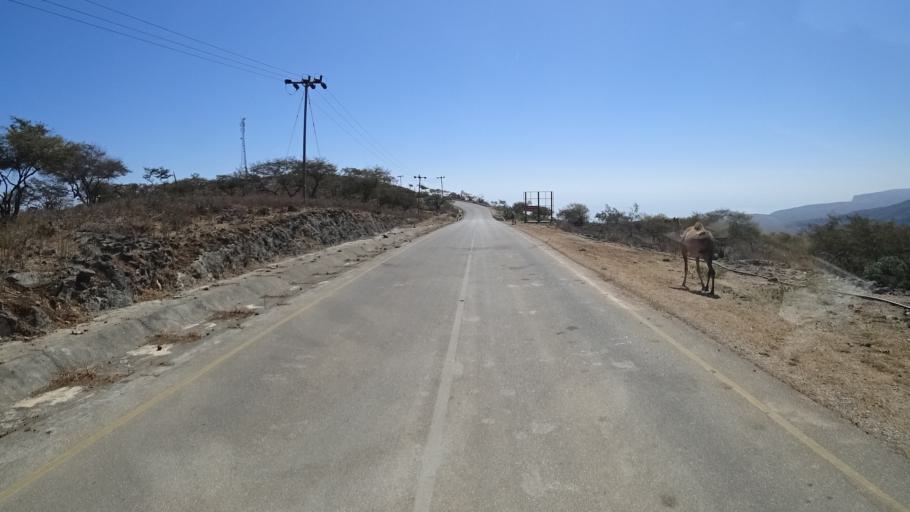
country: YE
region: Al Mahrah
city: Hawf
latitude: 16.7735
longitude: 53.3360
